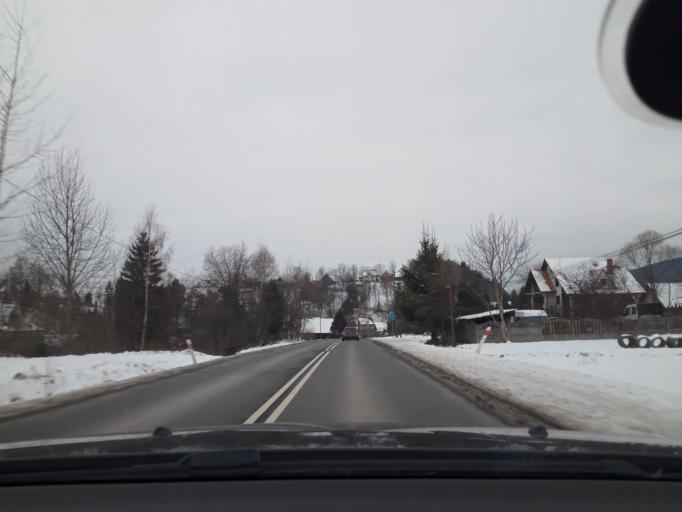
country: PL
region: Lesser Poland Voivodeship
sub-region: Powiat limanowski
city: Lubomierz
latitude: 49.6084
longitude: 20.1967
